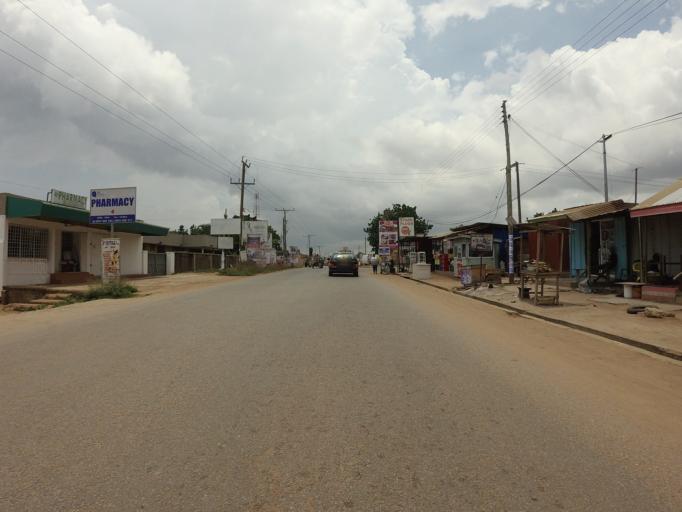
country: GH
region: Greater Accra
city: Medina Estates
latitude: 5.6863
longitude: -0.1675
